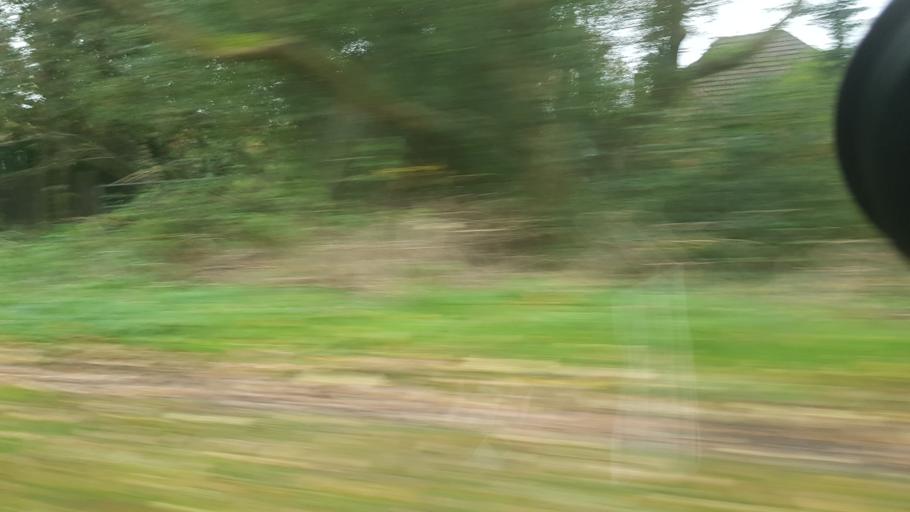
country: GB
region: England
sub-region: Bracknell Forest
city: Sandhurst
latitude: 51.3350
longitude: -0.8030
